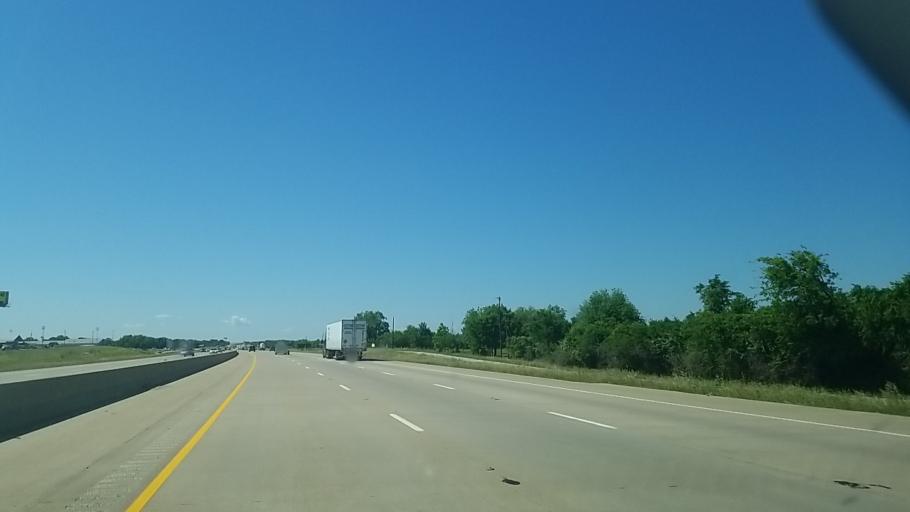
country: US
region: Texas
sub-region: Navarro County
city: Corsicana
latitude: 32.2237
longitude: -96.4859
